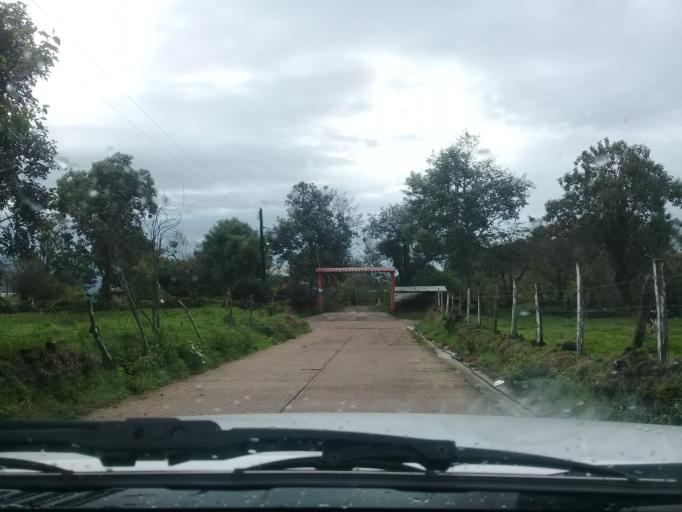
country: MX
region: Veracruz
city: Rafael Lucio
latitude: 19.6205
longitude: -96.9990
